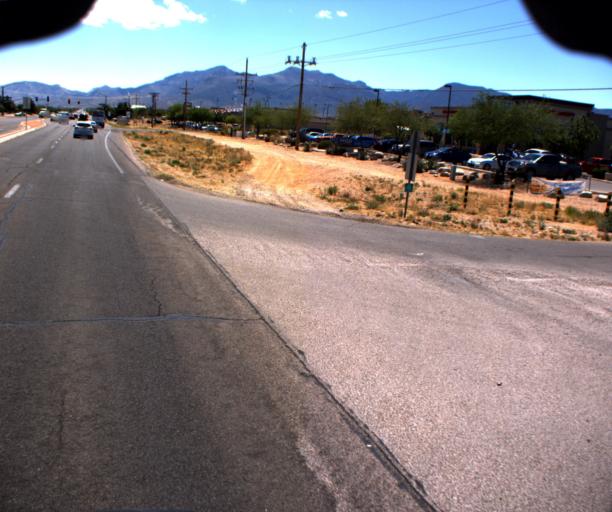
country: US
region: Arizona
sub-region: Cochise County
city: Sierra Vista
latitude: 31.5349
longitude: -110.2574
